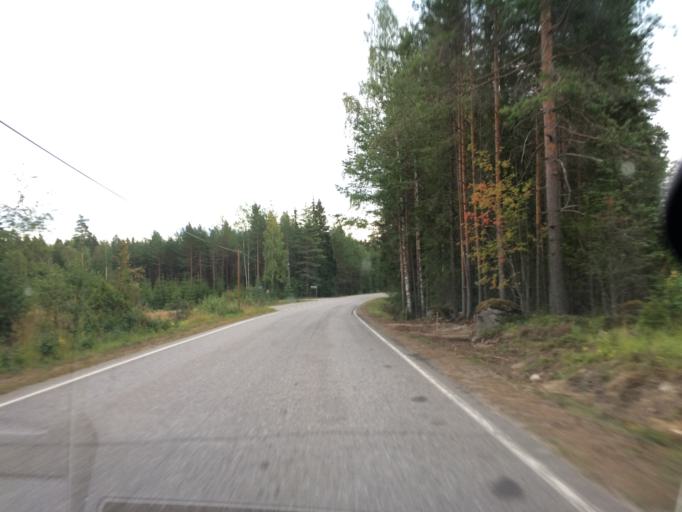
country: FI
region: Haeme
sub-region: Haemeenlinna
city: Tuulos
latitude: 61.1932
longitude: 24.7467
